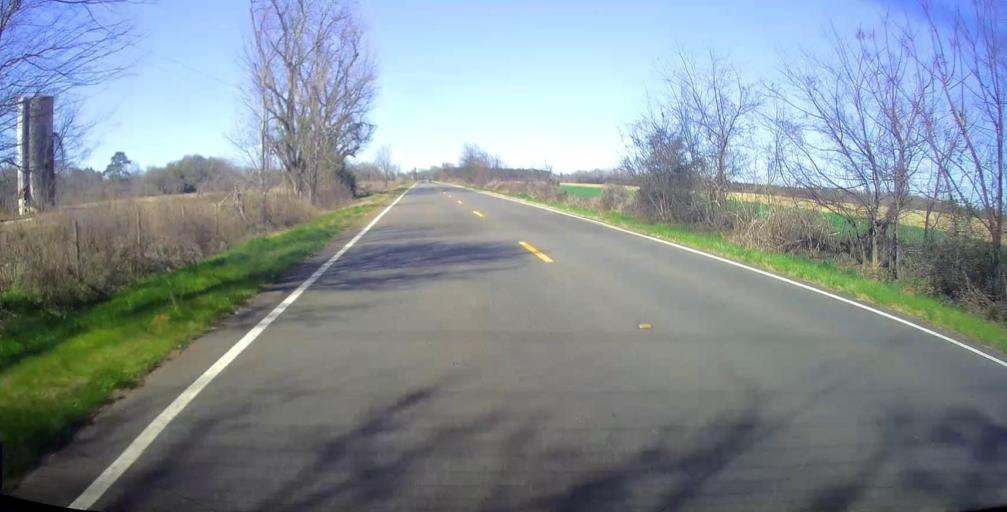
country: US
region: Georgia
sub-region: Macon County
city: Montezuma
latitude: 32.3810
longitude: -84.0151
